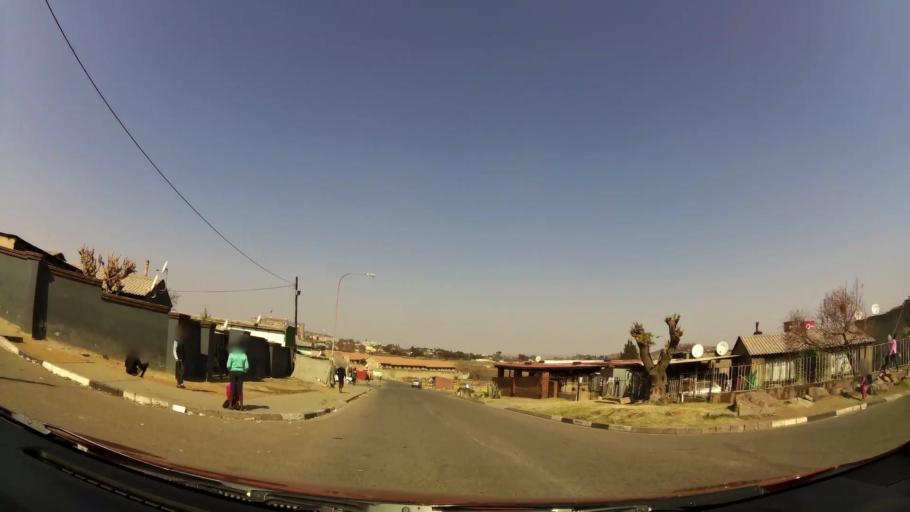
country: ZA
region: Gauteng
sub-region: City of Johannesburg Metropolitan Municipality
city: Soweto
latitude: -26.2493
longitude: 27.9368
